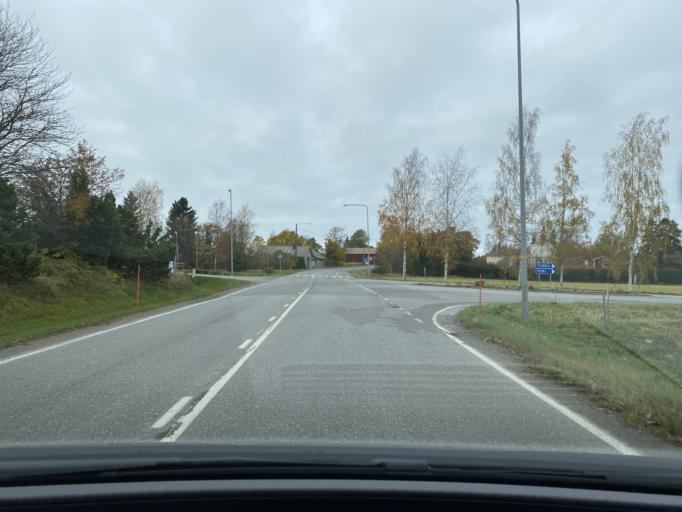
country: FI
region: Satakunta
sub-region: Pori
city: Luvia
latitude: 61.3627
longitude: 21.6205
